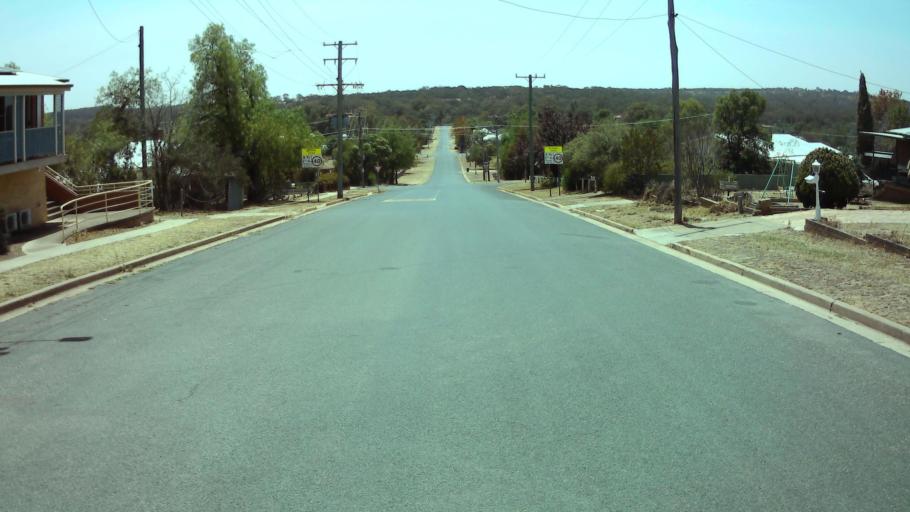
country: AU
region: New South Wales
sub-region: Weddin
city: Grenfell
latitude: -33.8943
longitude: 148.1684
